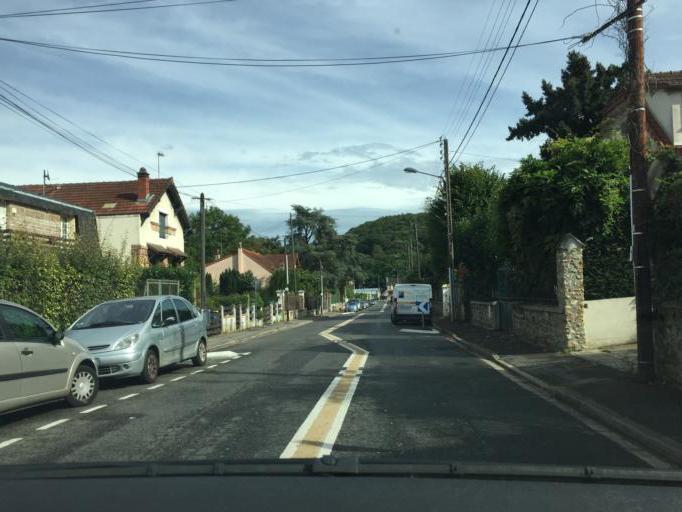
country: FR
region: Ile-de-France
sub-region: Departement de l'Essonne
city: Orsay
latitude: 48.6929
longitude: 2.1783
